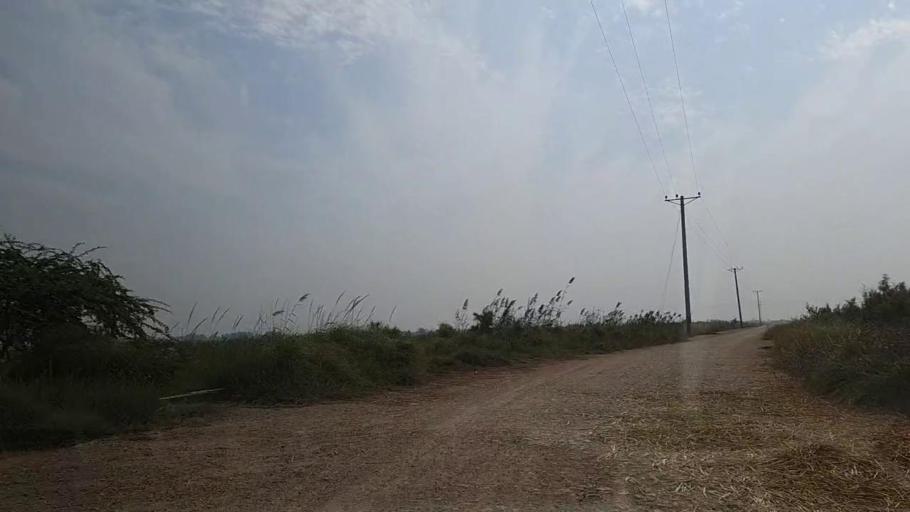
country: PK
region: Sindh
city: Mirpur Batoro
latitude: 24.6002
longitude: 68.2147
